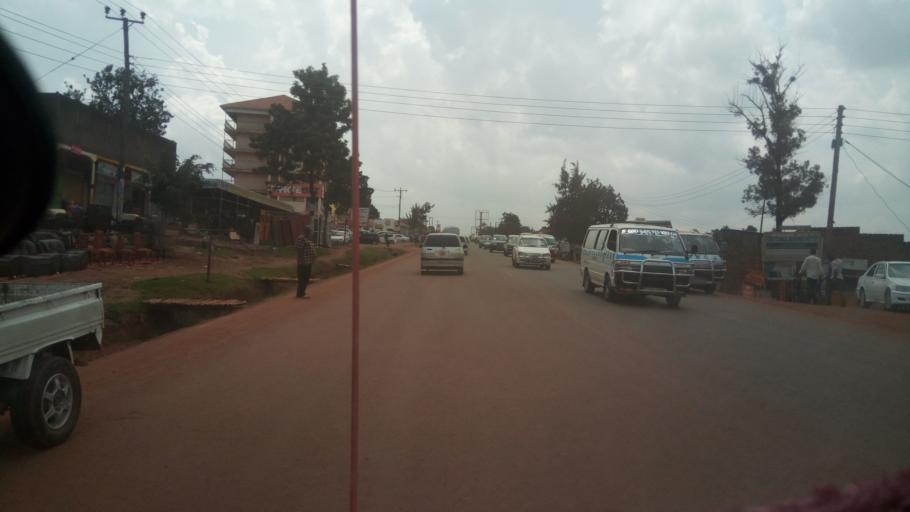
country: UG
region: Central Region
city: Kampala Central Division
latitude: 0.3527
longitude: 32.5368
